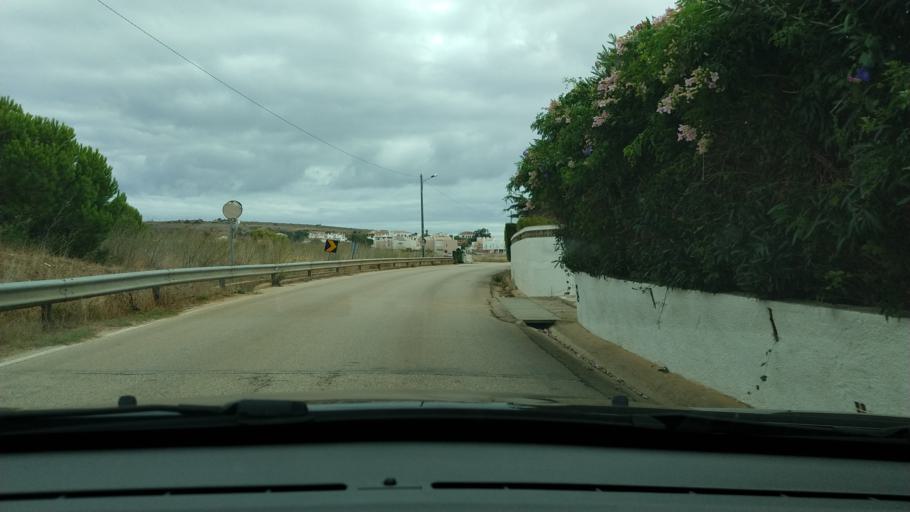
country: PT
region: Faro
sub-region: Lagos
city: Lagos
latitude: 37.0800
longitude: -8.7766
